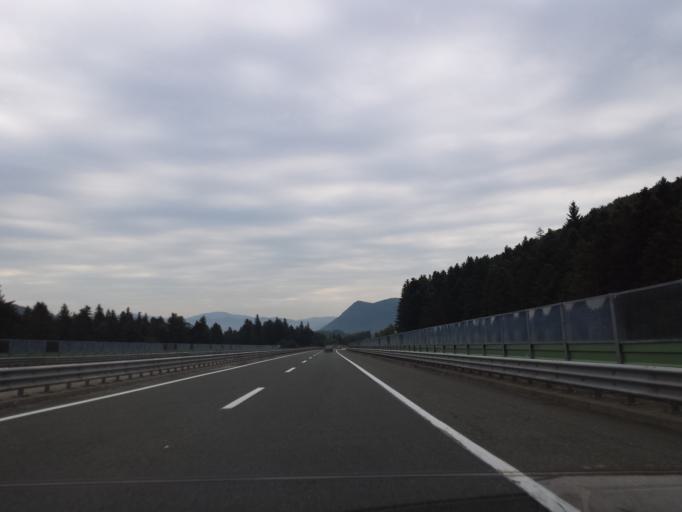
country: HR
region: Licko-Senjska
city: Otocac
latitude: 44.8470
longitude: 15.2361
